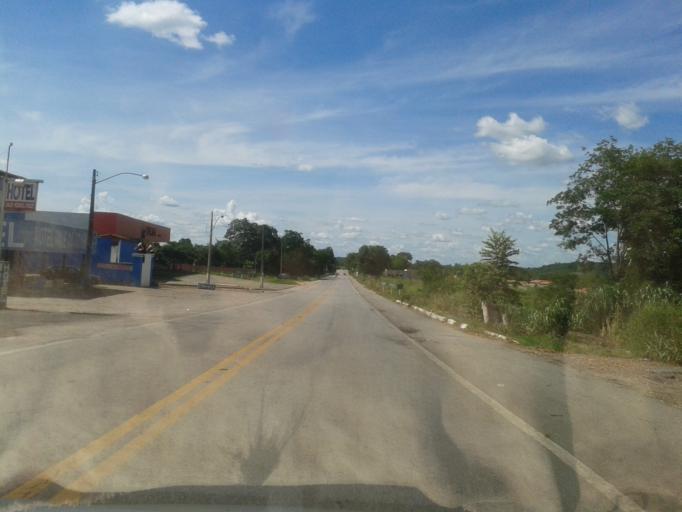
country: BR
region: Goias
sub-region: Itapuranga
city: Itapuranga
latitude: -15.4458
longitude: -50.3646
